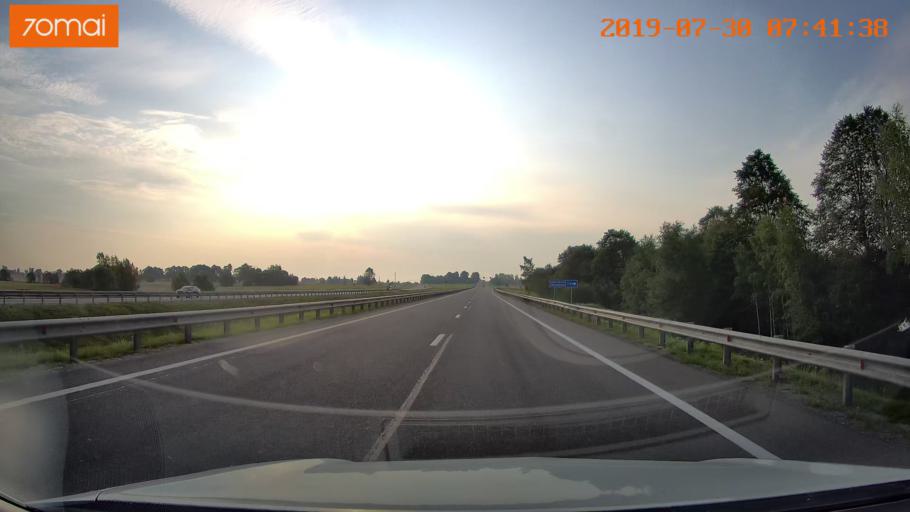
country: RU
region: Kaliningrad
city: Gvardeysk
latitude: 54.6483
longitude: 21.2568
